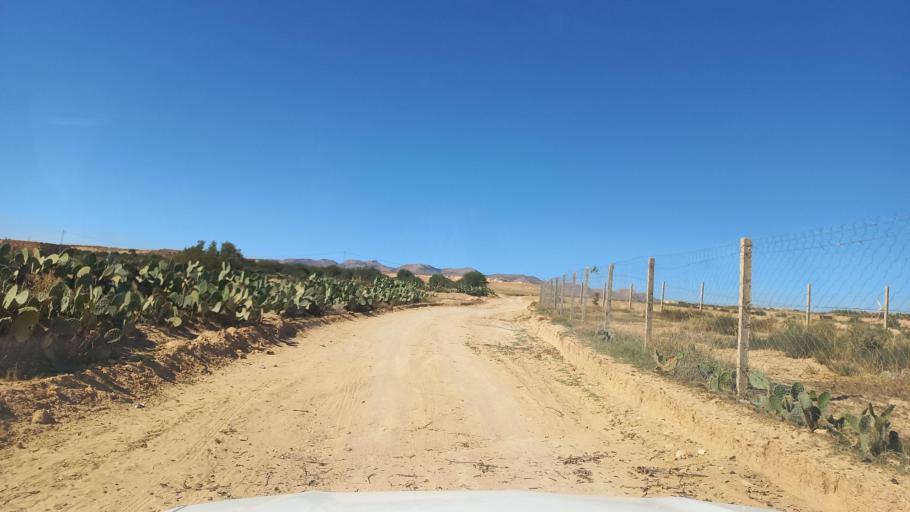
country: TN
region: Al Qasrayn
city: Sbiba
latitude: 35.3757
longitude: 9.0920
